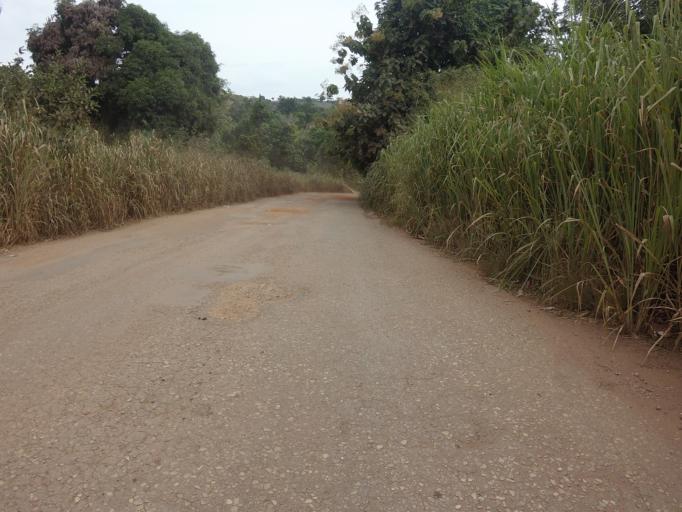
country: GH
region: Volta
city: Ho
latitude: 6.6854
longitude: 0.3453
